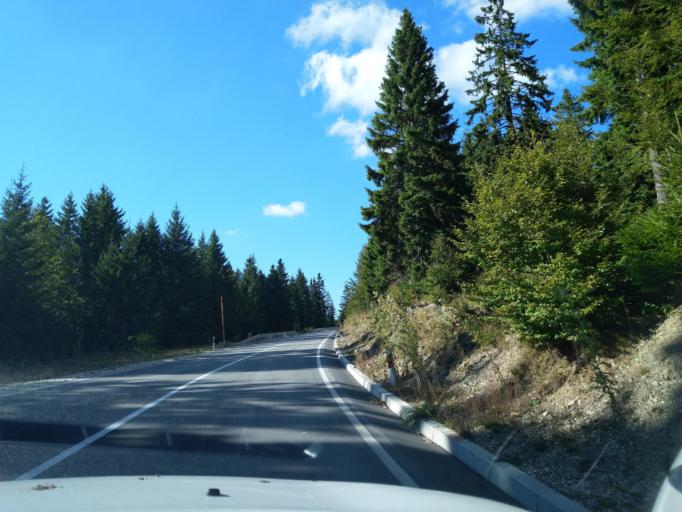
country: RS
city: Sokolovica
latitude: 43.3028
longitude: 20.3064
